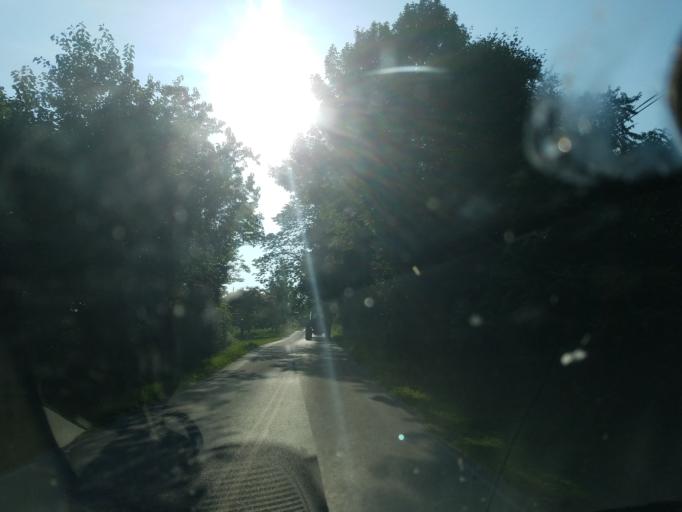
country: US
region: Ohio
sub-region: Adams County
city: West Union
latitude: 38.8832
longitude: -83.4976
